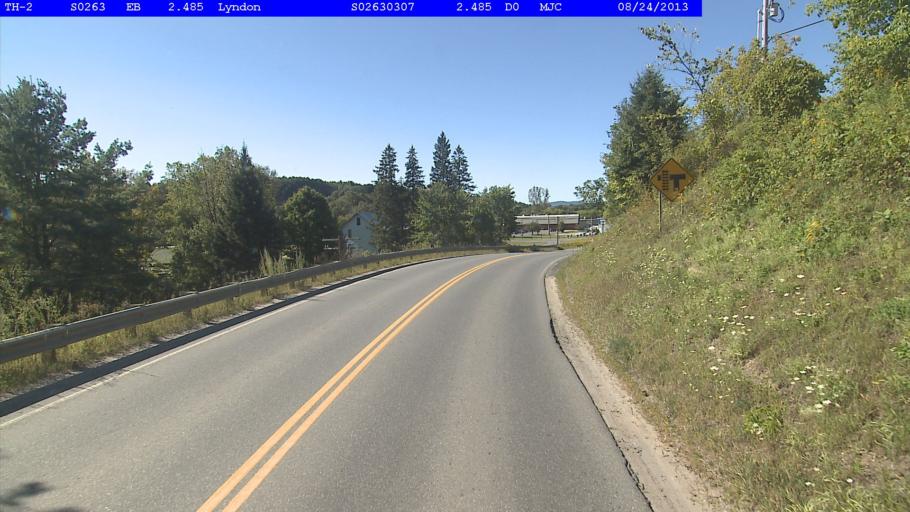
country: US
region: Vermont
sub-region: Caledonia County
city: Lyndon
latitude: 44.5180
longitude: -72.0013
